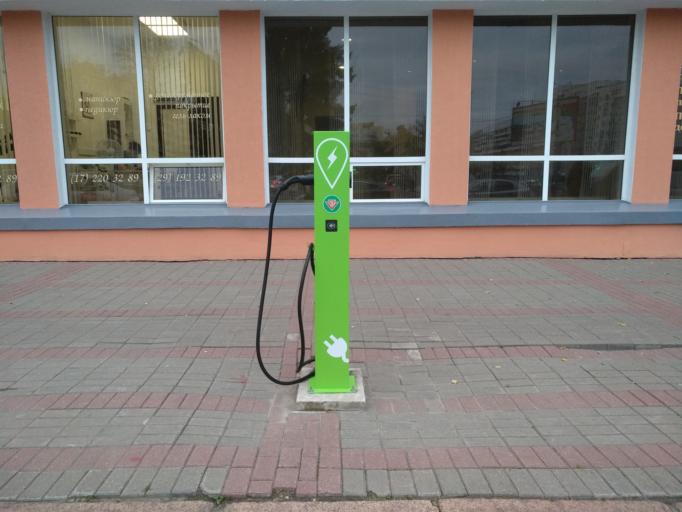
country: BY
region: Minsk
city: Minsk
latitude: 53.8783
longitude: 27.5335
